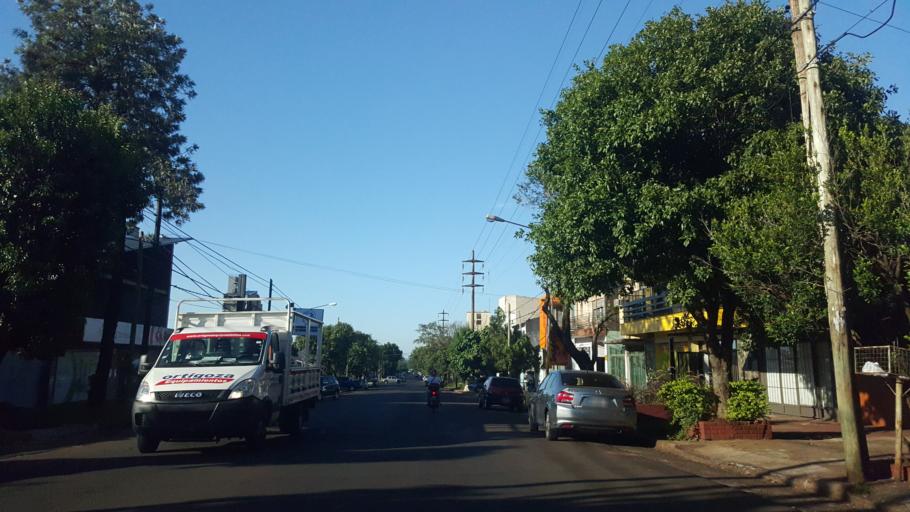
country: AR
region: Misiones
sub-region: Departamento de Capital
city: Posadas
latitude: -27.3717
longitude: -55.9058
